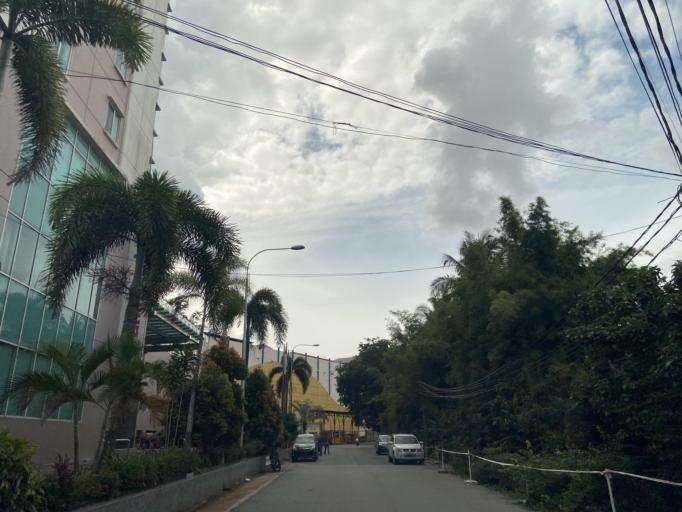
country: SG
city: Singapore
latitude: 1.1338
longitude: 104.0087
